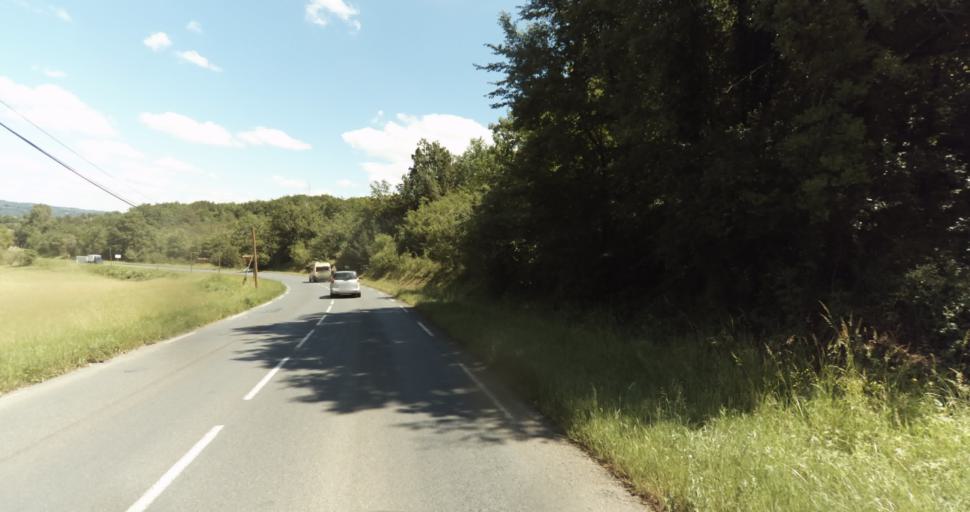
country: FR
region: Aquitaine
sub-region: Departement de la Dordogne
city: Le Bugue
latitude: 44.8424
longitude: 0.8838
